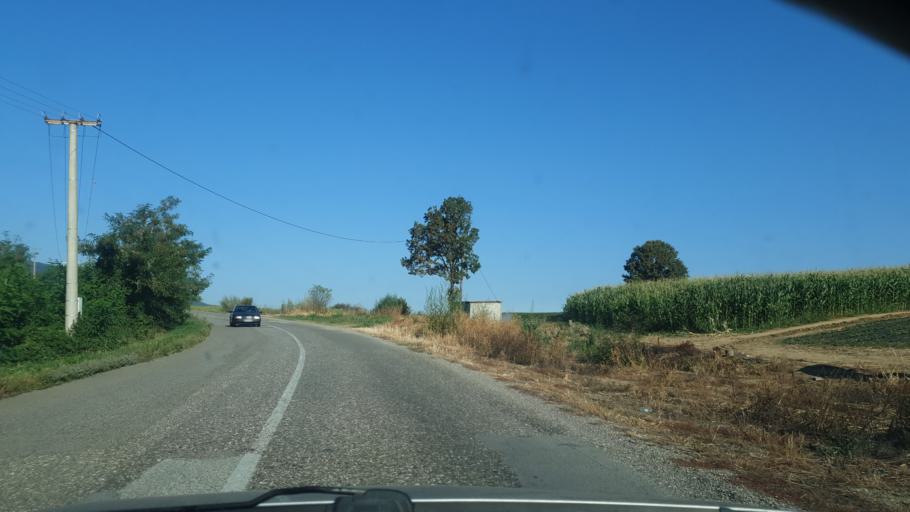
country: RS
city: Rumska
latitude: 44.5882
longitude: 19.5682
